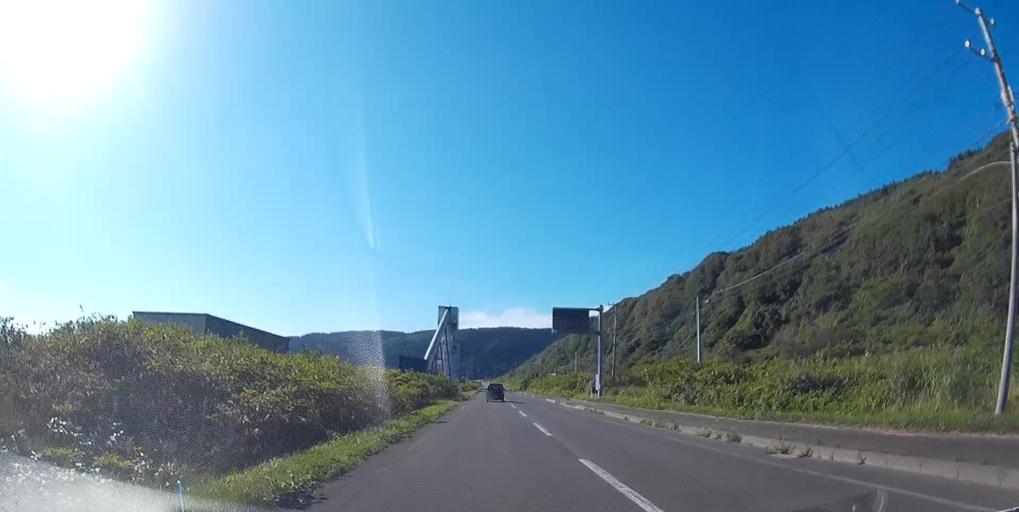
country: JP
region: Hokkaido
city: Kamiiso
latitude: 42.2154
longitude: 139.8718
